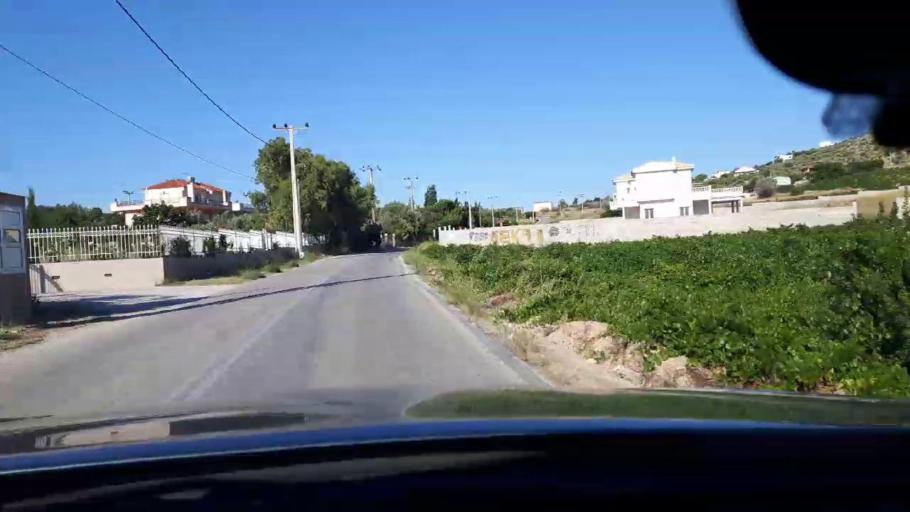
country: GR
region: Attica
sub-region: Nomarchia Anatolikis Attikis
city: Limin Mesoyaias
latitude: 37.8878
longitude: 23.9825
